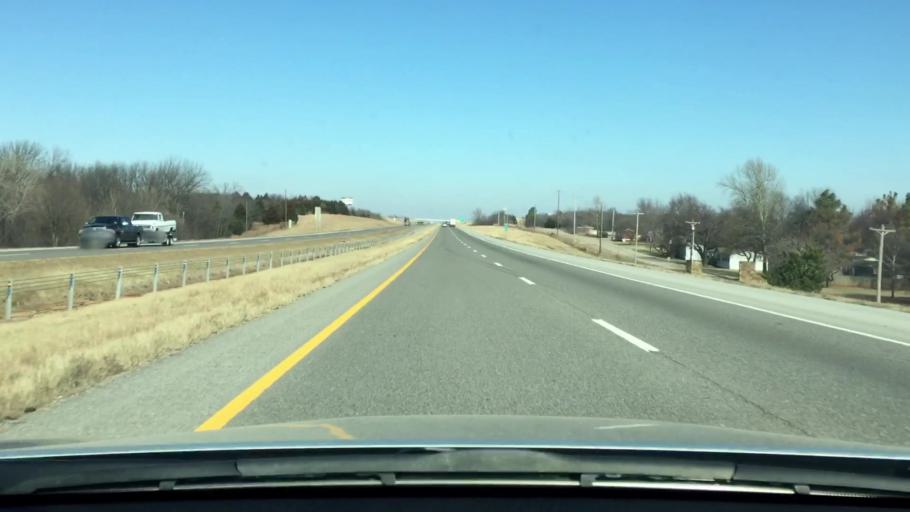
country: US
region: Oklahoma
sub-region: McClain County
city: Purcell
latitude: 34.9703
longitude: -97.3707
